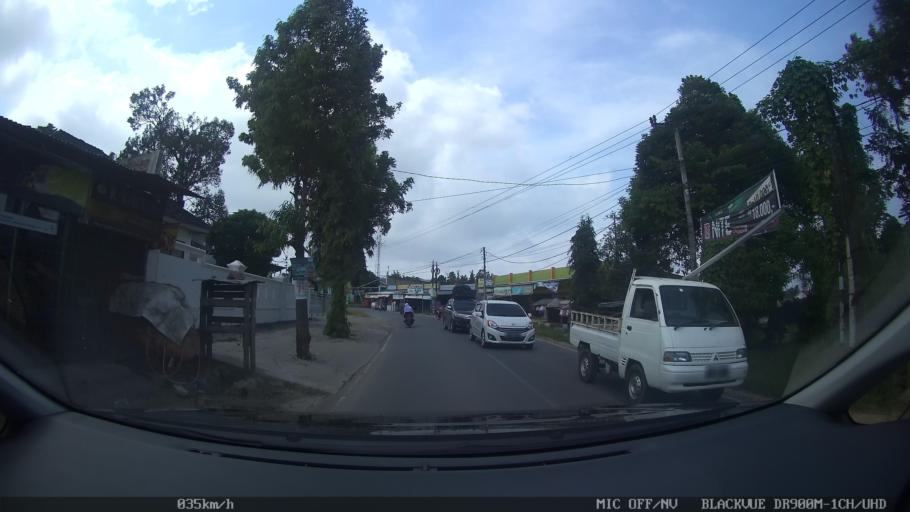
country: ID
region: Lampung
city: Kedaton
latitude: -5.3230
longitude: 105.2896
